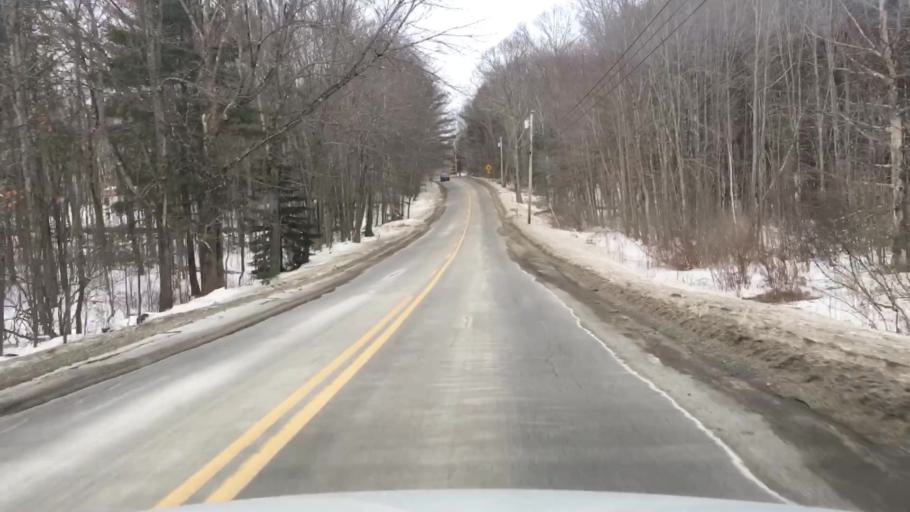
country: US
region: Maine
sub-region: Lincoln County
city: Whitefield
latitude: 44.2471
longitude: -69.6336
